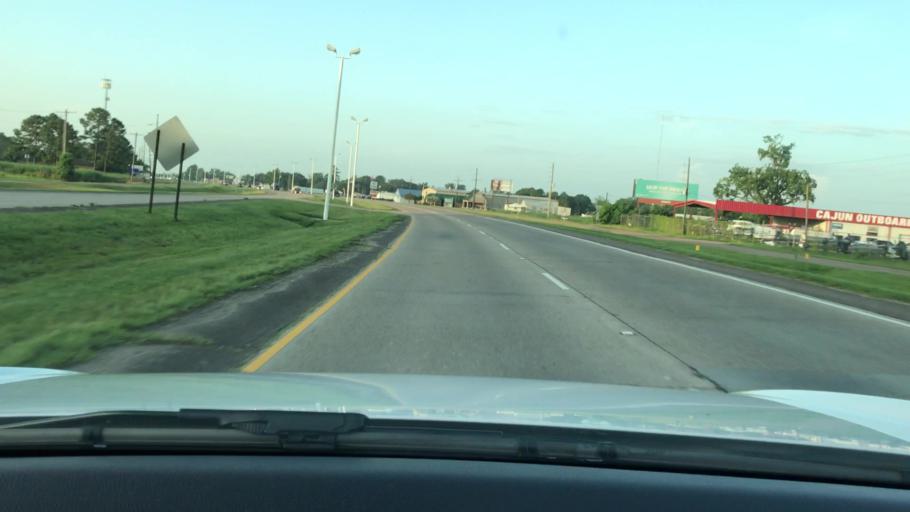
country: US
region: Louisiana
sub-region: West Baton Rouge Parish
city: Addis
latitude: 30.3633
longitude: -91.2611
